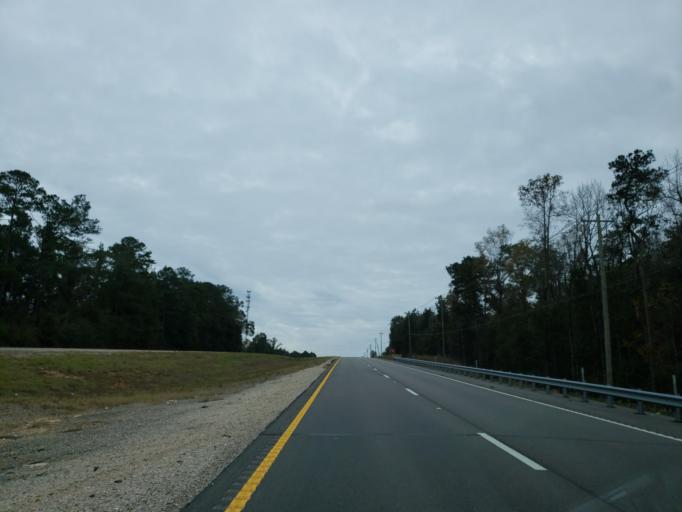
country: US
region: Mississippi
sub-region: Forrest County
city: Hattiesburg
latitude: 31.2262
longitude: -89.2683
